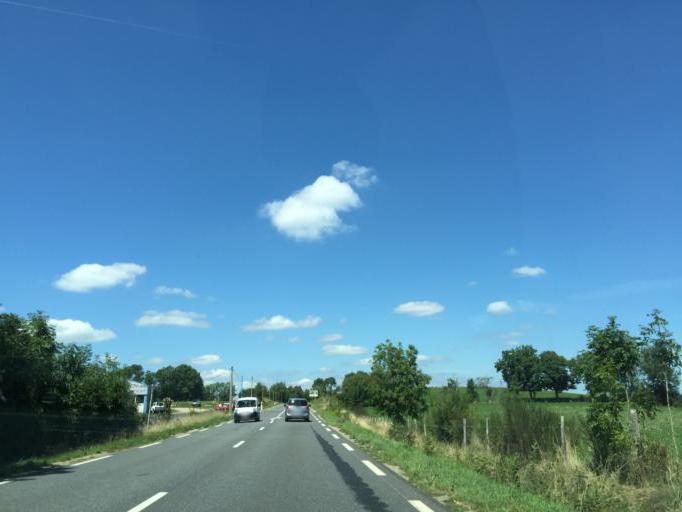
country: FR
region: Midi-Pyrenees
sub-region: Departement de l'Aveyron
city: Espalion
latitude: 44.5973
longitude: 2.7965
